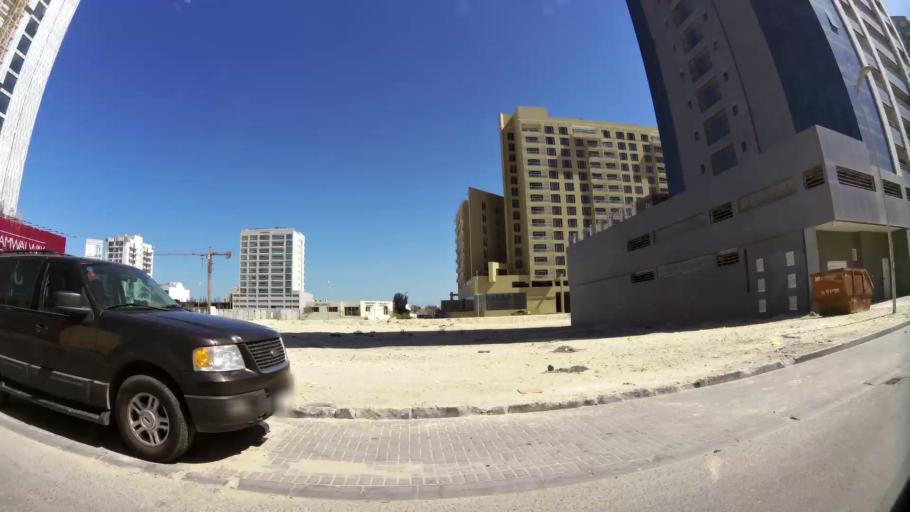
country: BH
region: Muharraq
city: Al Hadd
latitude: 26.2878
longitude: 50.6648
